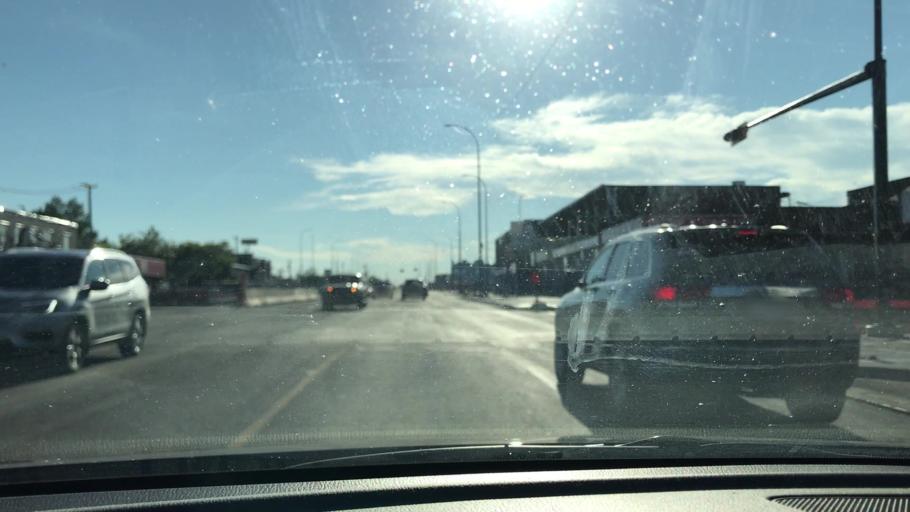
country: CA
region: Alberta
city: Calgary
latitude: 51.0379
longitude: -113.9725
